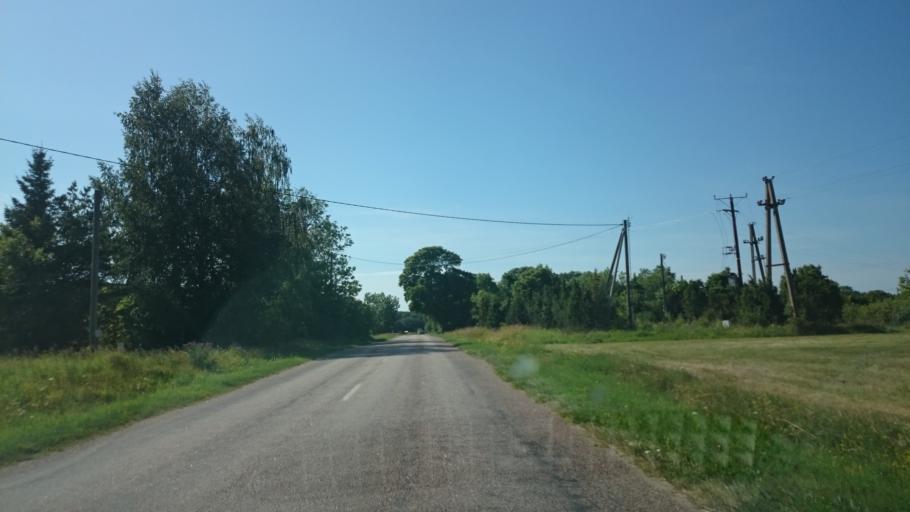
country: EE
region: Saare
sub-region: Orissaare vald
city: Orissaare
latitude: 58.5723
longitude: 22.7258
